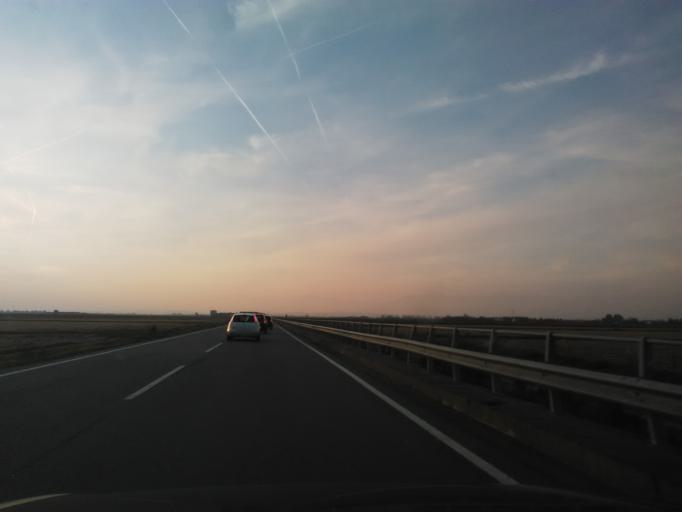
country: IT
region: Piedmont
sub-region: Provincia di Vercelli
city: Olcenengo
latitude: 45.3358
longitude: 8.3033
